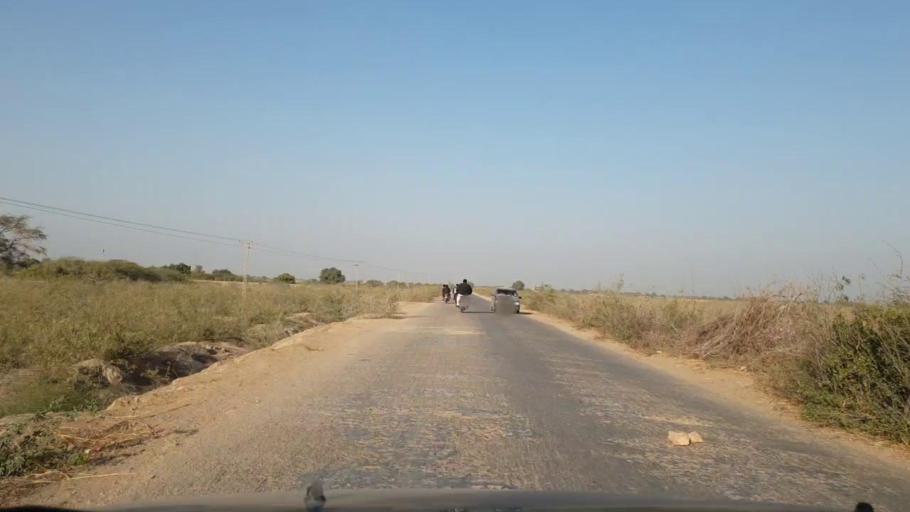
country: PK
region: Sindh
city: Chambar
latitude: 25.2449
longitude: 68.7886
